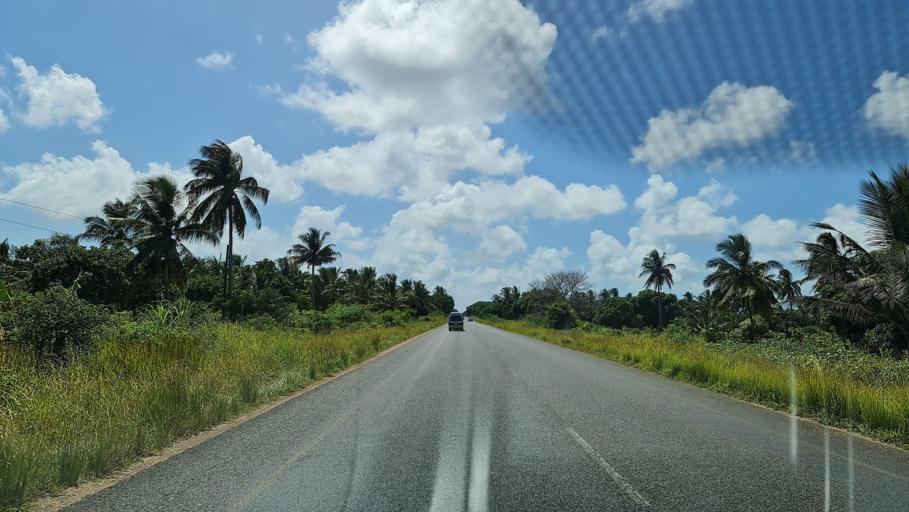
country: MZ
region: Inhambane
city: Maxixe
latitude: -24.5414
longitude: 34.9126
